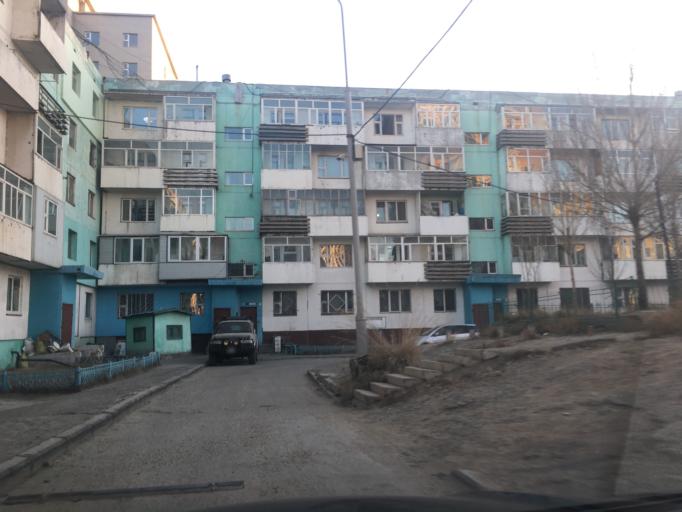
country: MN
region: Ulaanbaatar
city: Ulaanbaatar
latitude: 47.9191
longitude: 106.8794
